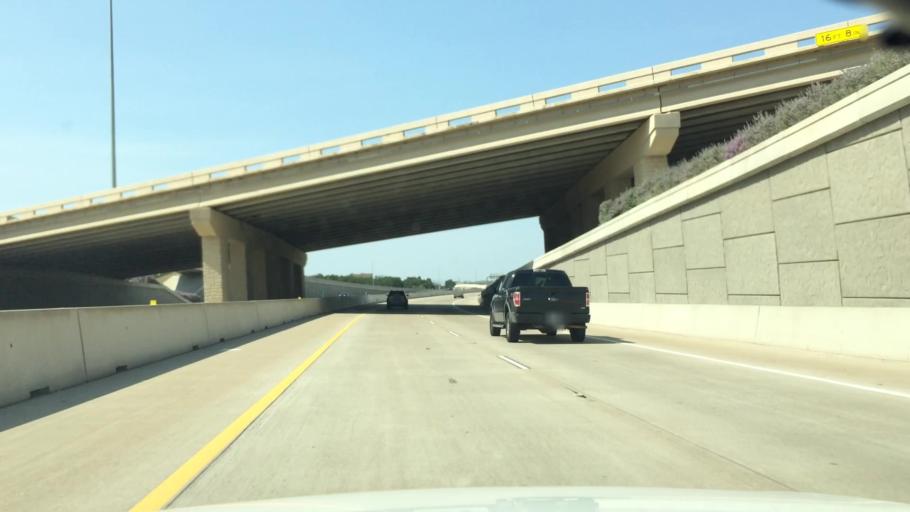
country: US
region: Texas
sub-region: Dallas County
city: Grand Prairie
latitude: 32.7641
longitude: -97.0290
